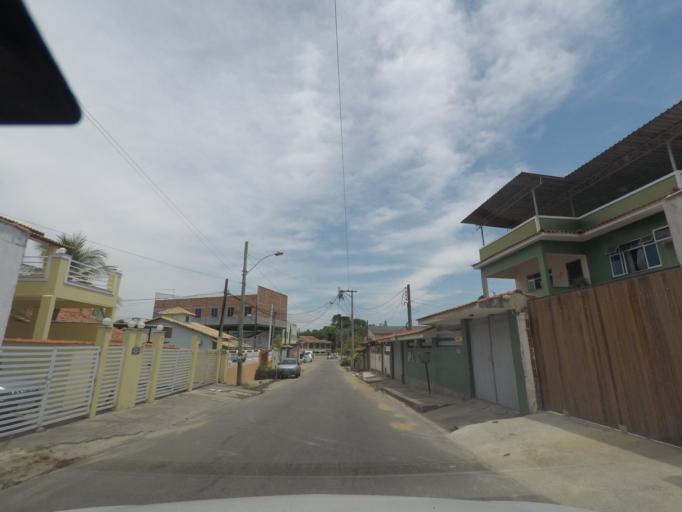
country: BR
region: Rio de Janeiro
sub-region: Marica
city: Marica
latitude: -22.9247
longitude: -42.8181
